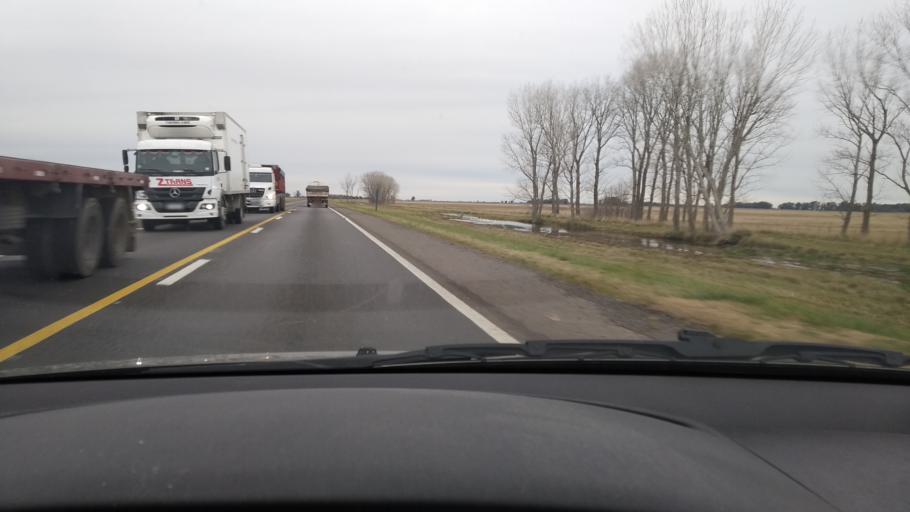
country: AR
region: Buenos Aires
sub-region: Partido de Las Flores
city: Las Flores
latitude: -36.1618
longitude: -59.2234
